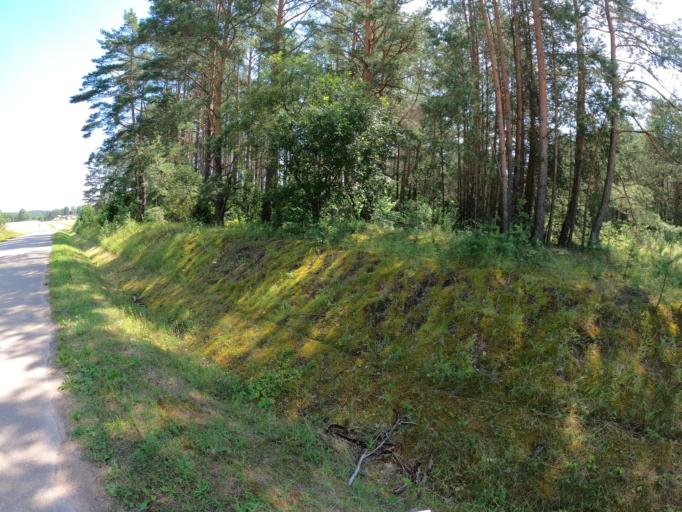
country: LT
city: Lazdijai
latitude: 54.0931
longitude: 23.5253
